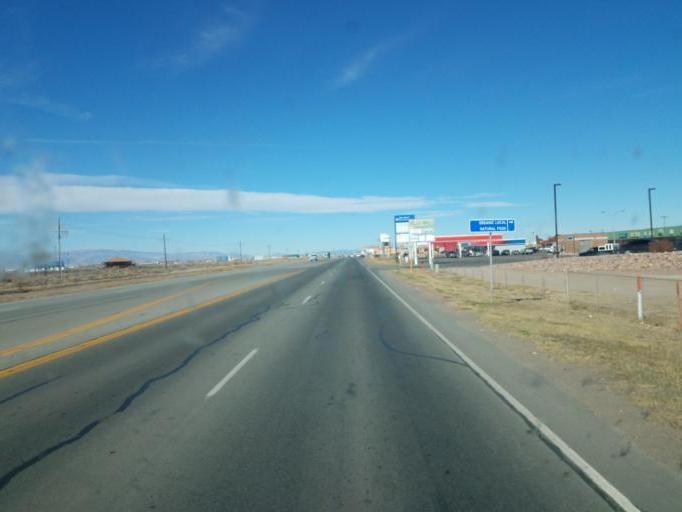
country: US
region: Colorado
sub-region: Alamosa County
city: Alamosa
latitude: 37.4773
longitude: -105.8995
